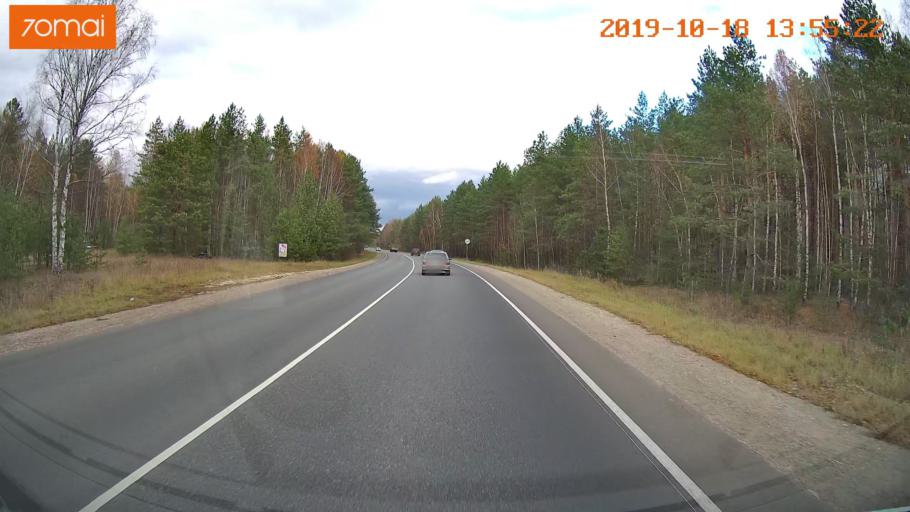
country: RU
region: Rjazan
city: Spas-Klepiki
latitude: 55.0513
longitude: 40.0227
